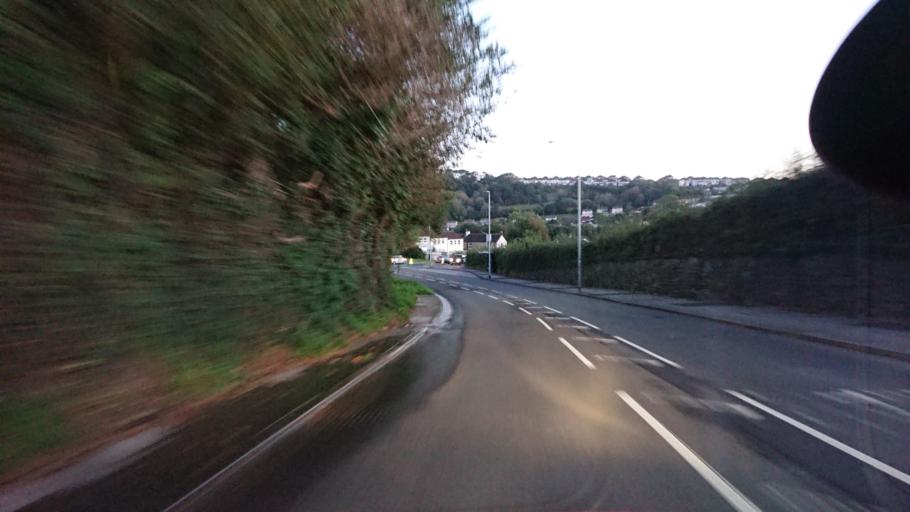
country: GB
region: England
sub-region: Plymouth
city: Plymouth
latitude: 50.3994
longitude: -4.1134
